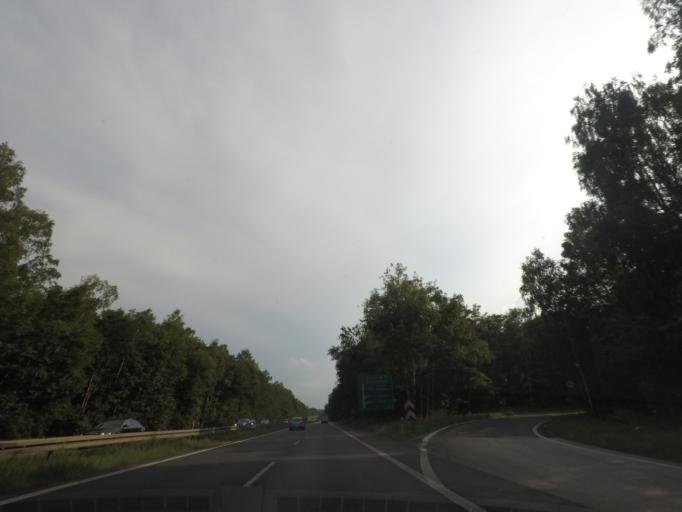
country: PL
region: Silesian Voivodeship
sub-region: Dabrowa Gornicza
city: Dabrowa Gornicza
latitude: 50.3254
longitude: 19.2408
